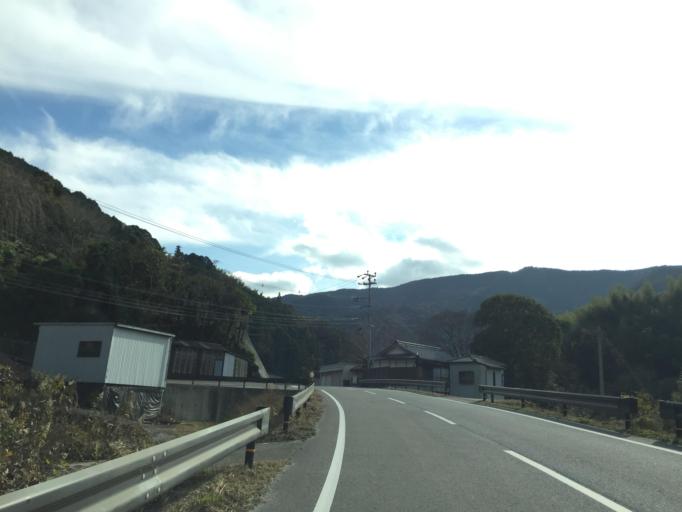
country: JP
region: Wakayama
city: Iwade
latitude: 34.1420
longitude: 135.3853
